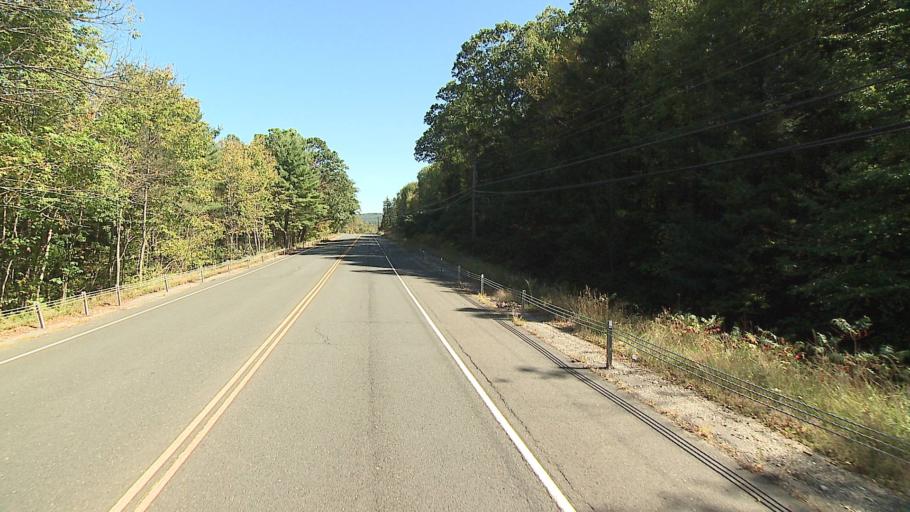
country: US
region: Connecticut
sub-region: Litchfield County
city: Northwest Harwinton
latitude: 41.8268
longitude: -73.0451
